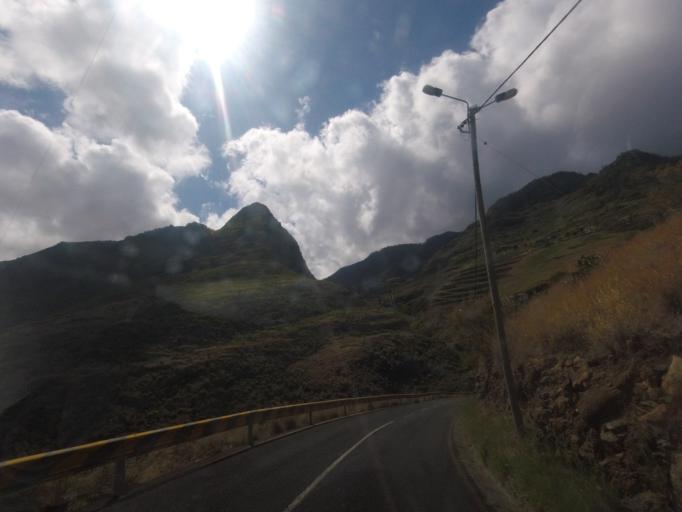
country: PT
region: Madeira
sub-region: Machico
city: Canical
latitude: 32.7357
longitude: -16.7451
